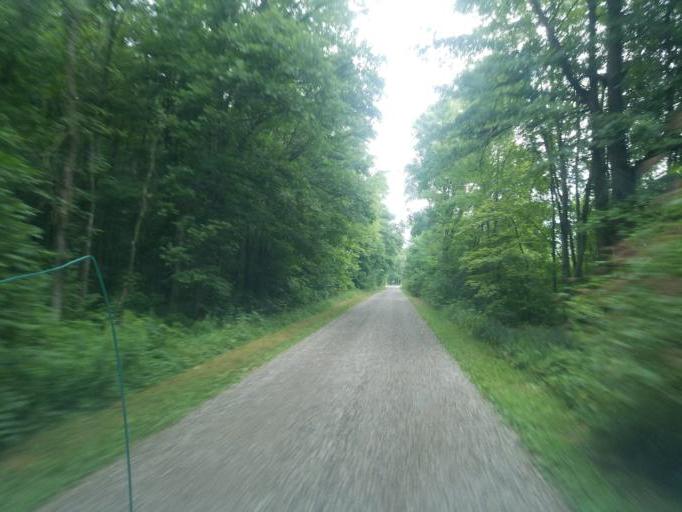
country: US
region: Ohio
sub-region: Defiance County
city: Hicksville
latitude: 41.3657
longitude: -84.8040
